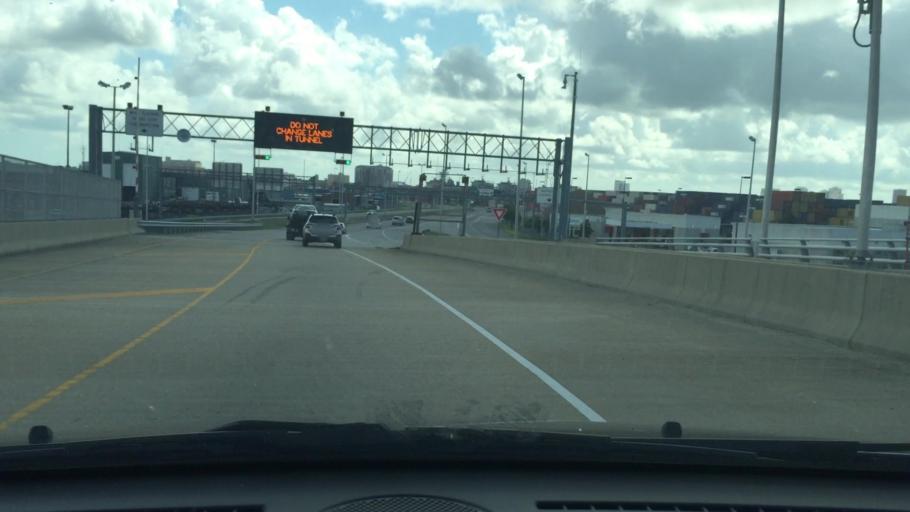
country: US
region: Virginia
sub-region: City of Portsmouth
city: Portsmouth
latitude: 36.8519
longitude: -76.3277
